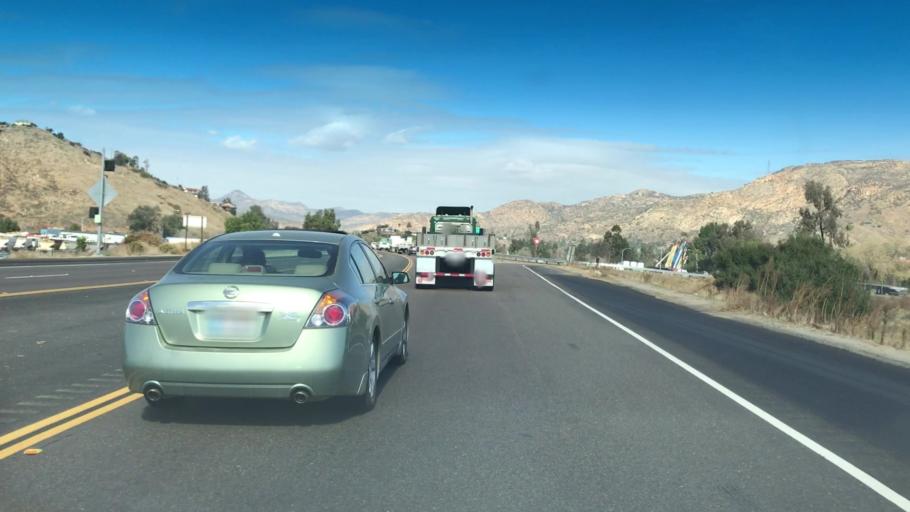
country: US
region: California
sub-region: San Diego County
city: Lakeside
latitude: 32.8652
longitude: -116.9223
